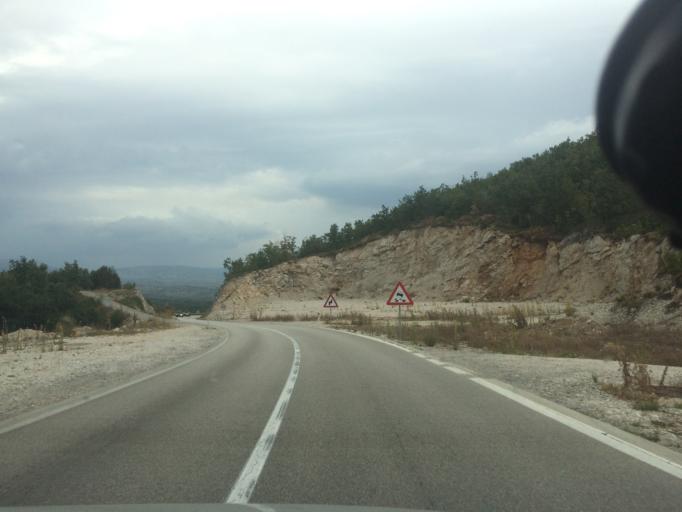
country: ME
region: Kotor
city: Risan
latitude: 42.7147
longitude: 18.6072
